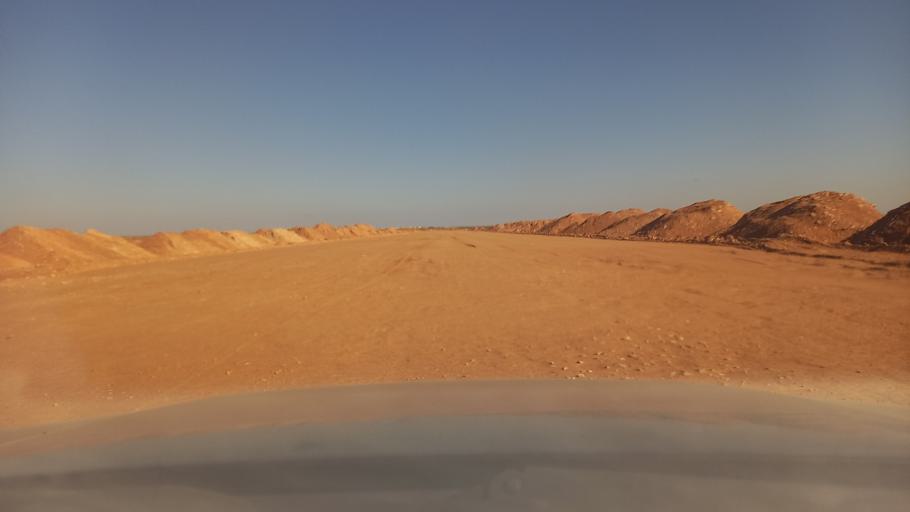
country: TN
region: Madanin
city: Medenine
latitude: 33.1642
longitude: 10.5211
